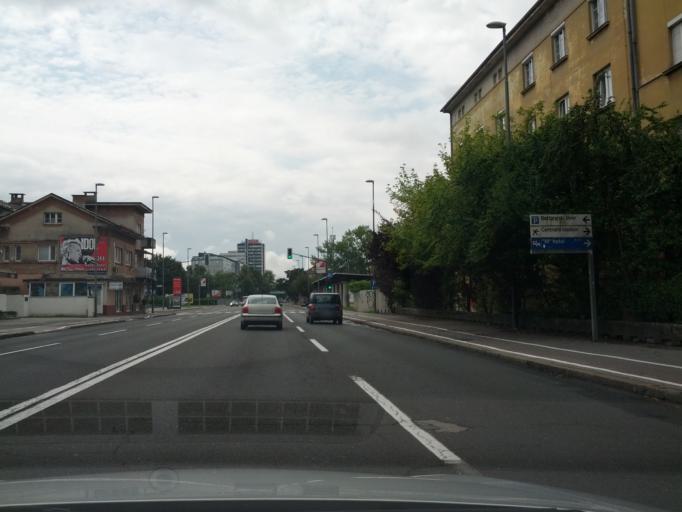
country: SI
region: Ljubljana
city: Ljubljana
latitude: 46.0706
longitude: 14.5105
